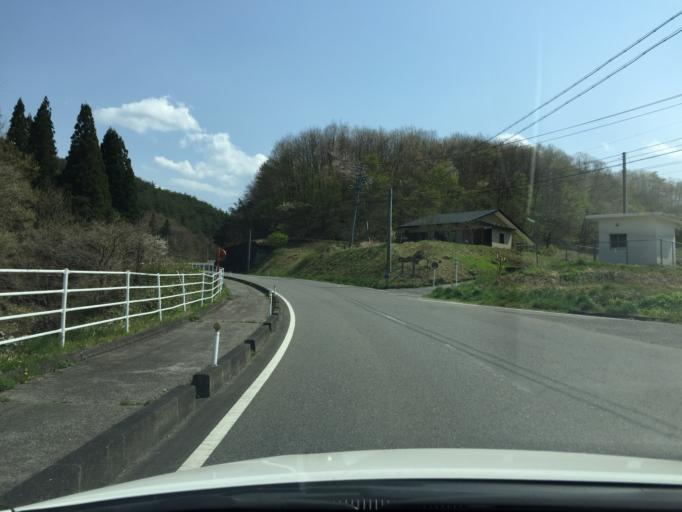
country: JP
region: Fukushima
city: Funehikimachi-funehiki
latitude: 37.4242
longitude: 140.7901
